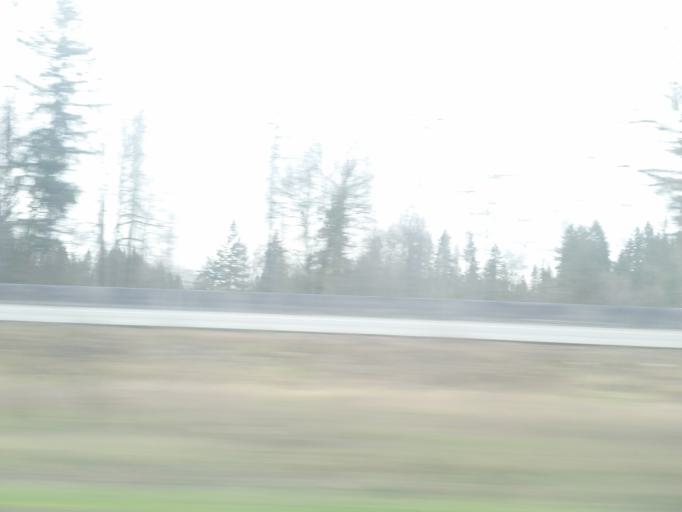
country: US
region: Washington
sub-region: Snohomish County
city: Maltby
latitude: 47.8123
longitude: -122.0828
